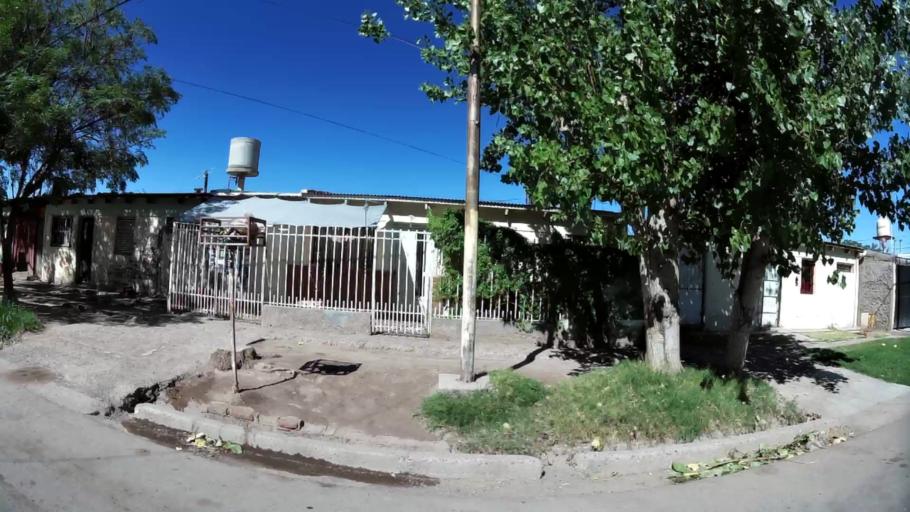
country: AR
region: Mendoza
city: Las Heras
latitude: -32.8256
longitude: -68.8155
